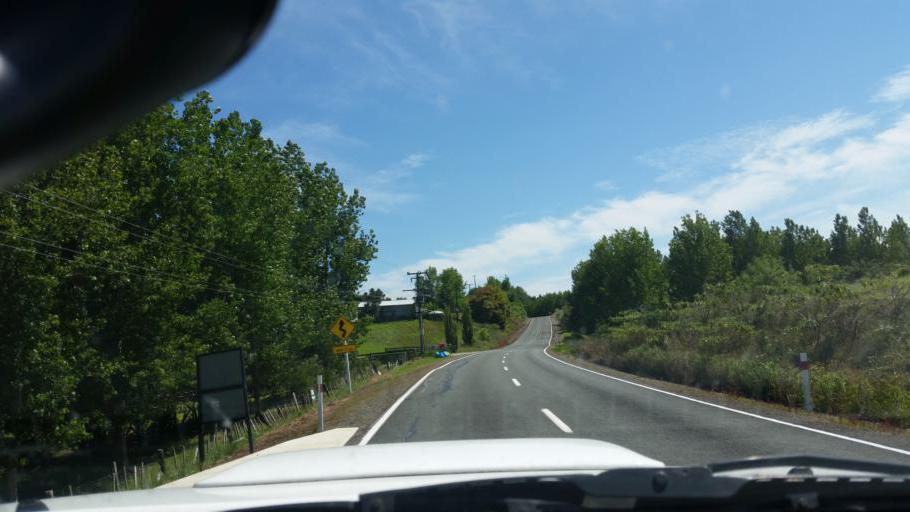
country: NZ
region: Auckland
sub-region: Auckland
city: Wellsford
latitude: -36.2146
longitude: 174.3901
